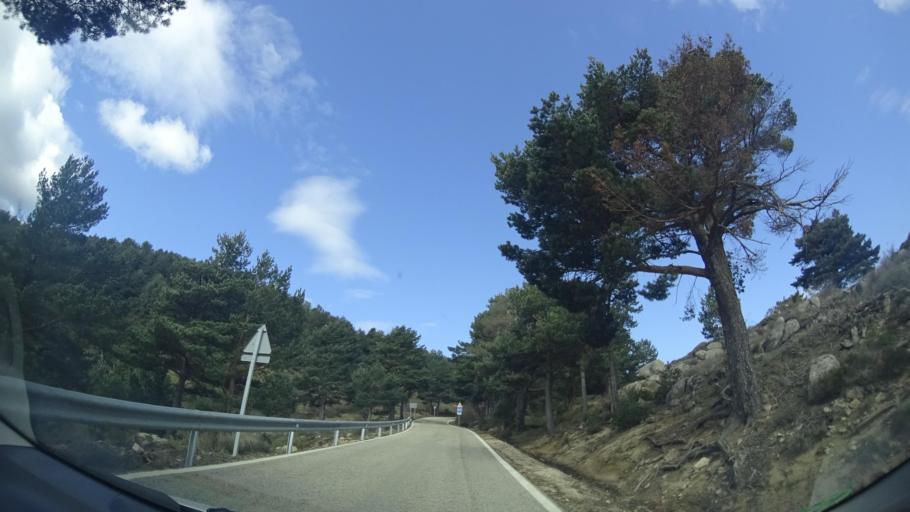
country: ES
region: Madrid
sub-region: Provincia de Madrid
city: Canencia
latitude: 40.8671
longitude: -3.7624
